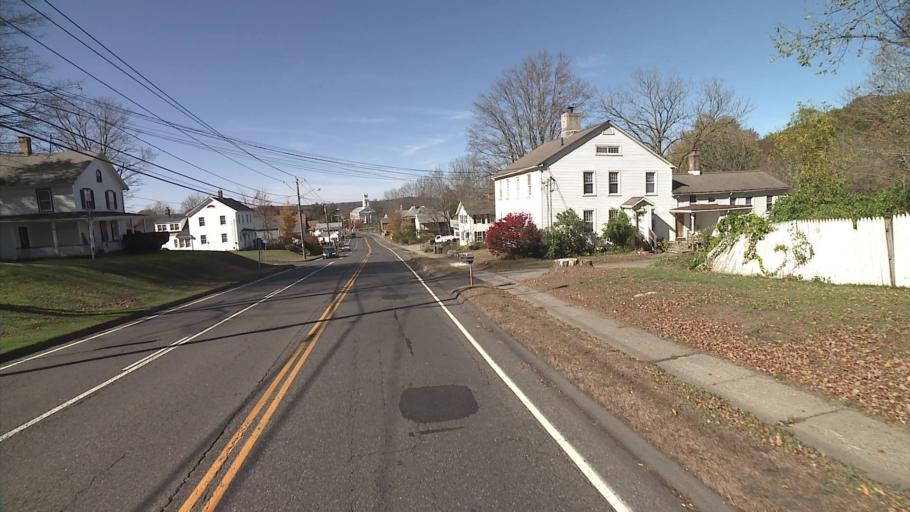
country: US
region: Connecticut
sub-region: Litchfield County
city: Plymouth
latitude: 41.6716
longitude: -73.0497
